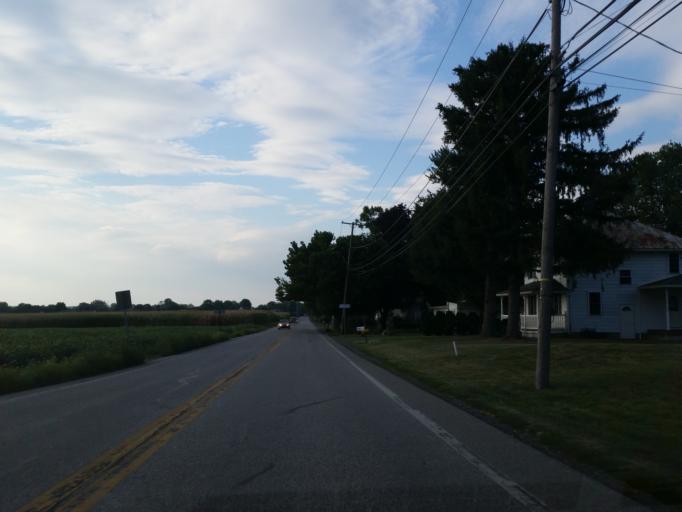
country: US
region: Pennsylvania
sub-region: Lebanon County
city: Campbelltown
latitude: 40.2913
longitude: -76.5752
